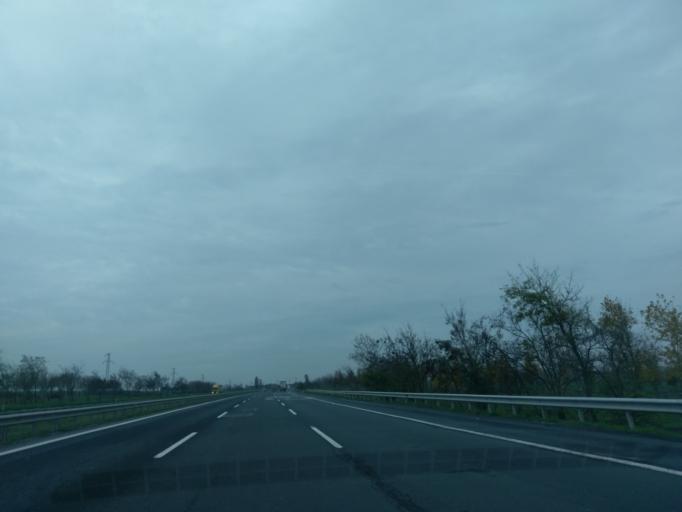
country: TR
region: Istanbul
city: Canta
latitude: 41.1322
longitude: 28.1566
